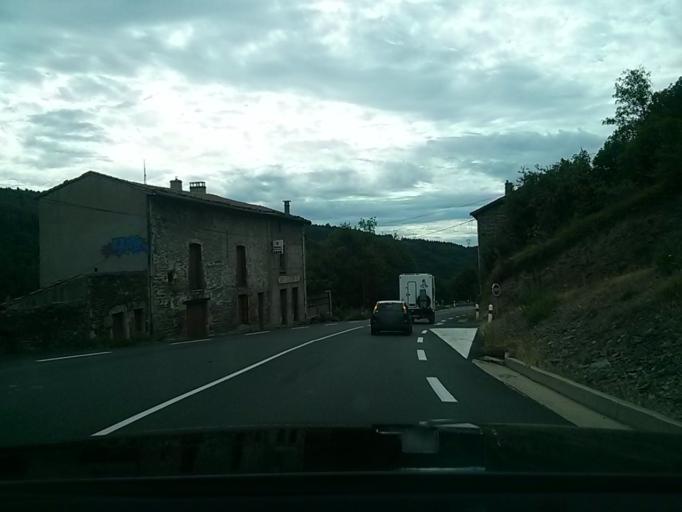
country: FR
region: Rhone-Alpes
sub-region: Departement de la Loire
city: Saint-Etienne
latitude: 45.4007
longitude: 4.4142
